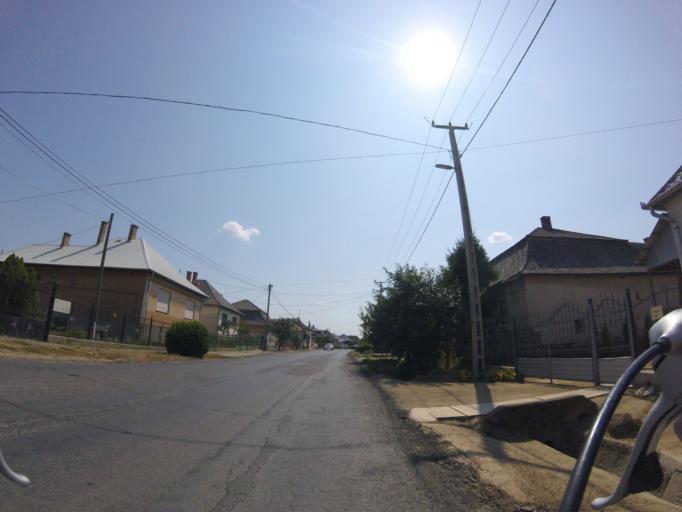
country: HU
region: Szabolcs-Szatmar-Bereg
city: Anarcs
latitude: 48.1585
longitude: 22.1393
